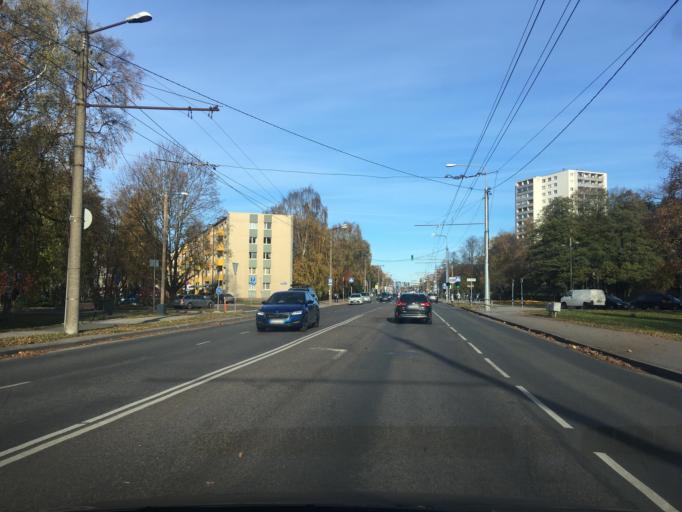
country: EE
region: Harju
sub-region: Tallinna linn
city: Tallinn
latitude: 59.4062
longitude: 24.6826
